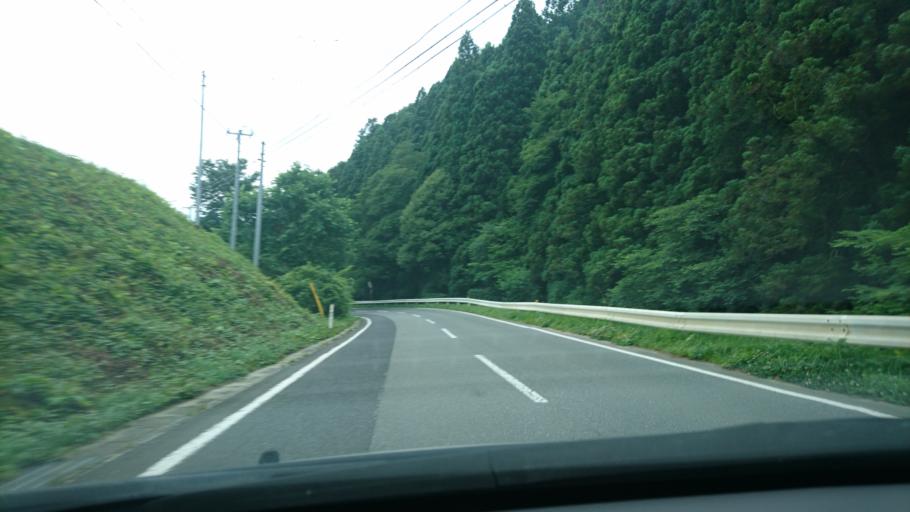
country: JP
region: Iwate
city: Ichinoseki
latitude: 38.8655
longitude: 141.4252
